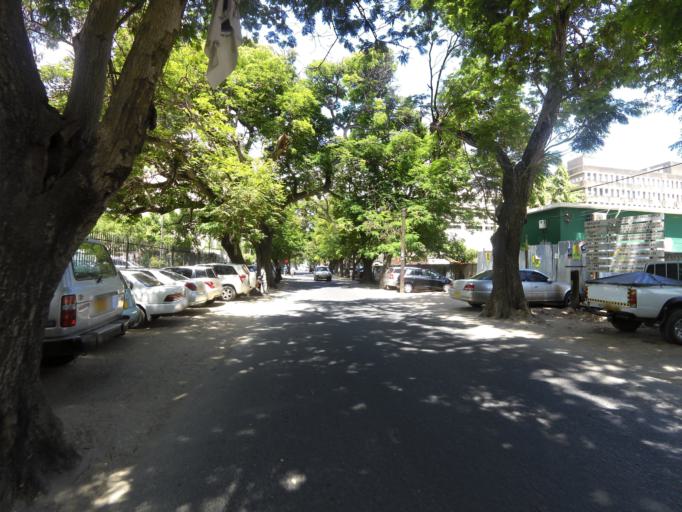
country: TZ
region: Dar es Salaam
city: Dar es Salaam
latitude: -6.8156
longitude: 39.2929
